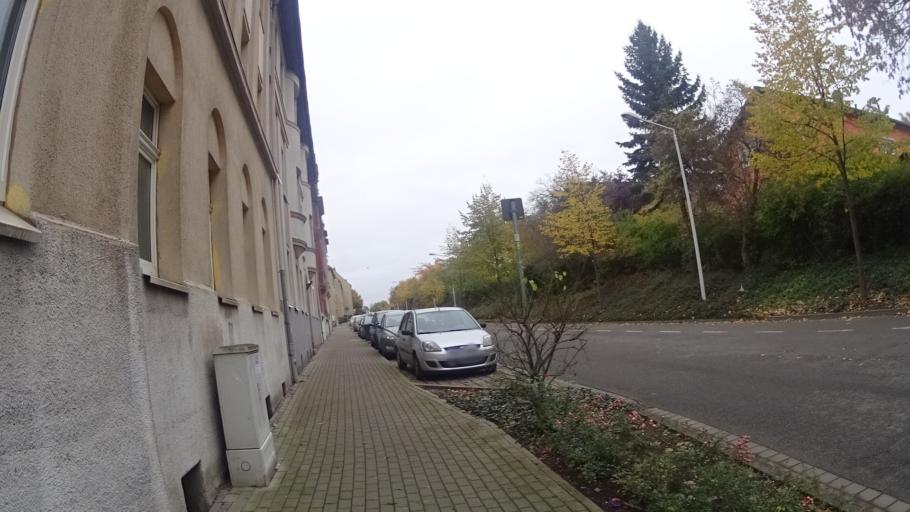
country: DE
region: Thuringia
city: Arnstadt
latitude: 50.8394
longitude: 10.9395
